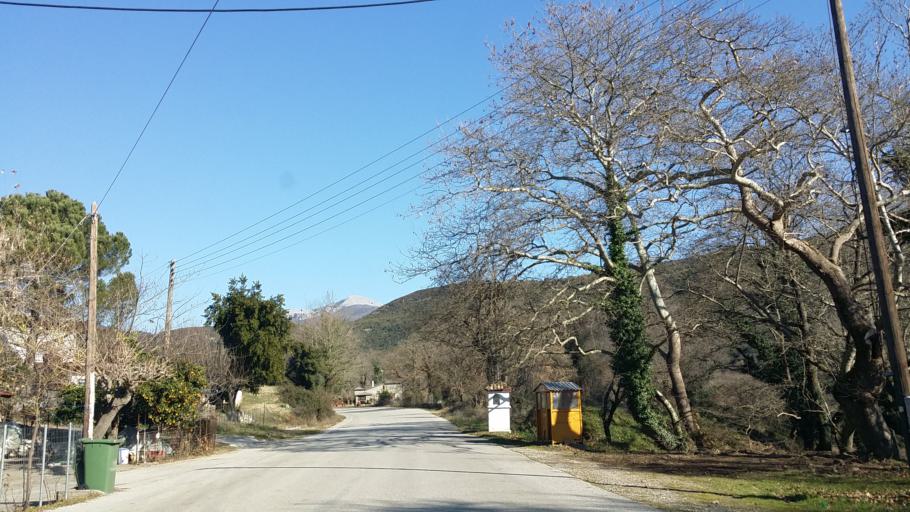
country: GR
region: West Greece
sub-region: Nomos Aitolias kai Akarnanias
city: Sardinia
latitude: 38.9080
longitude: 21.3506
